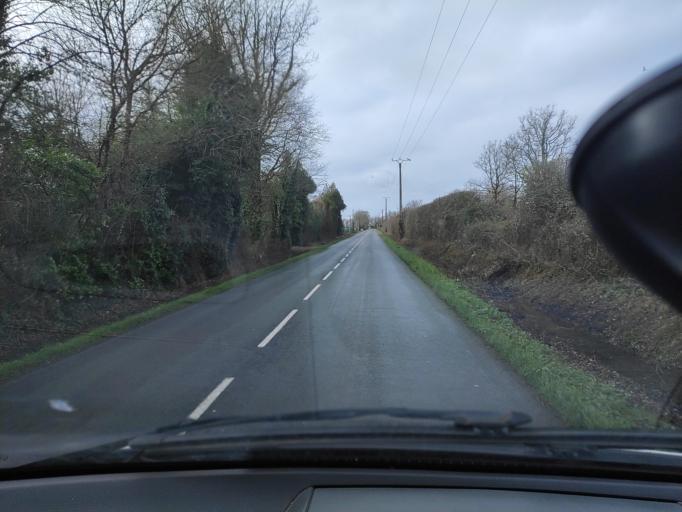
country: FR
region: Pays de la Loire
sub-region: Departement de la Vendee
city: Nieul-le-Dolent
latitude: 46.5690
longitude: -1.4878
